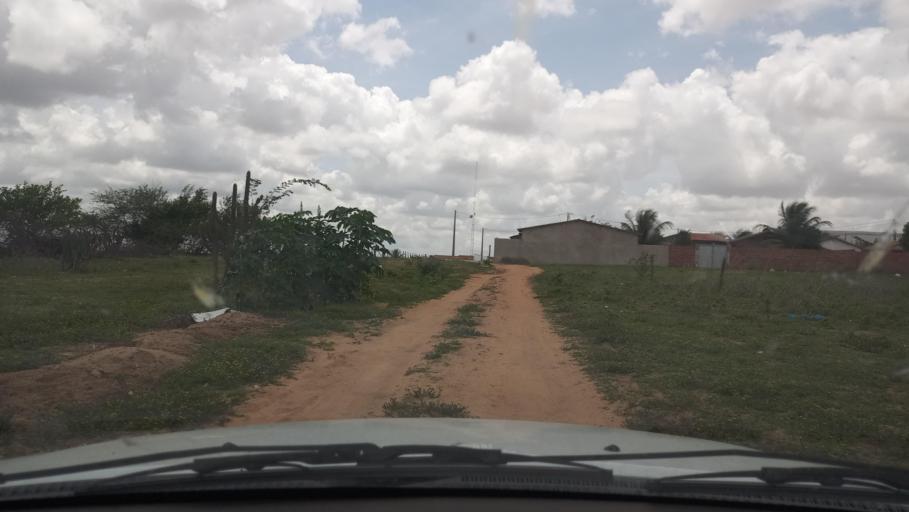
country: BR
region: Rio Grande do Norte
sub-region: Tangara
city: Tangara
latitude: -6.0950
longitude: -35.7081
